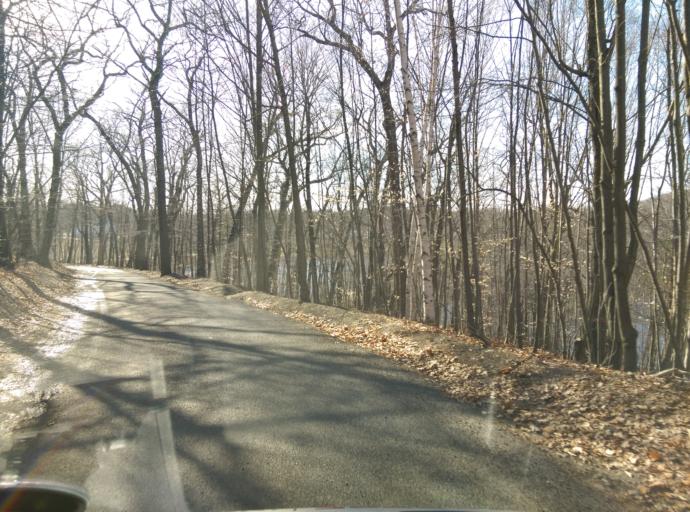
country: US
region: Massachusetts
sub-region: Essex County
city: Haverhill
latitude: 42.7899
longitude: -71.0637
